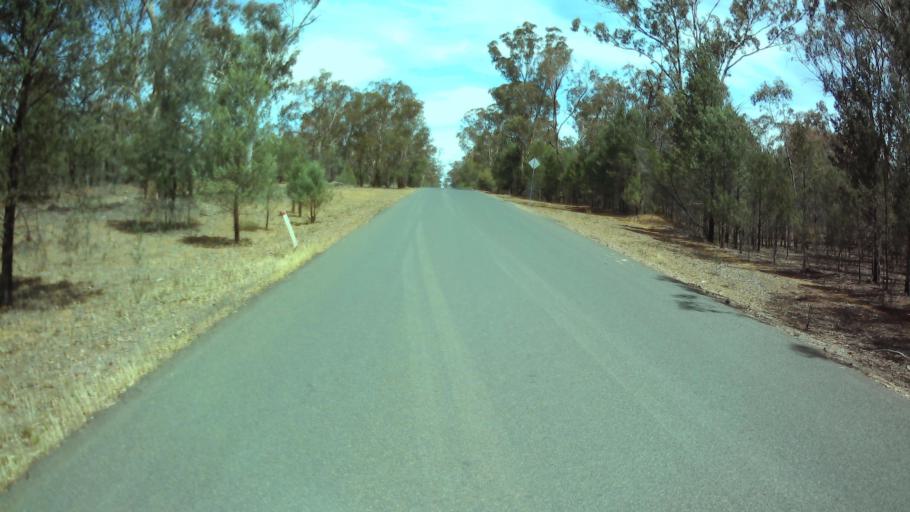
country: AU
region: New South Wales
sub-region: Weddin
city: Grenfell
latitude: -33.8494
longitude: 147.7439
